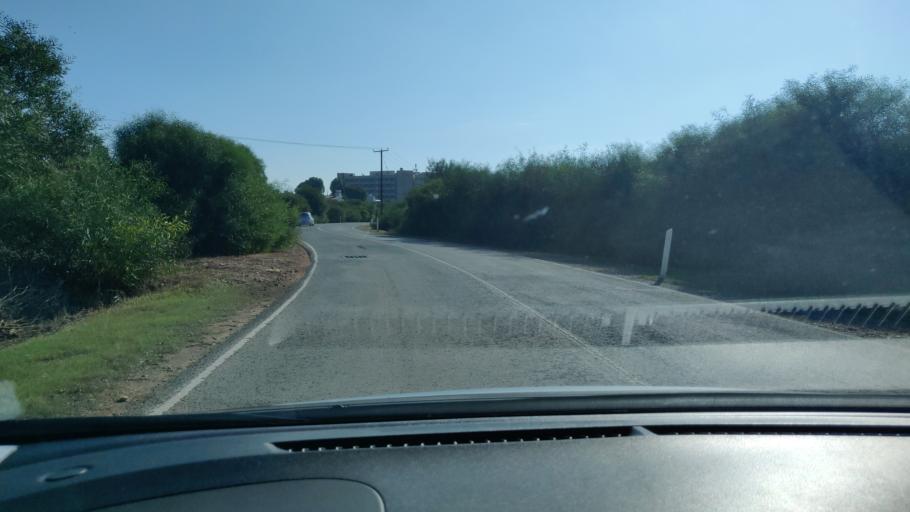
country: CY
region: Ammochostos
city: Protaras
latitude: 34.9866
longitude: 34.0640
